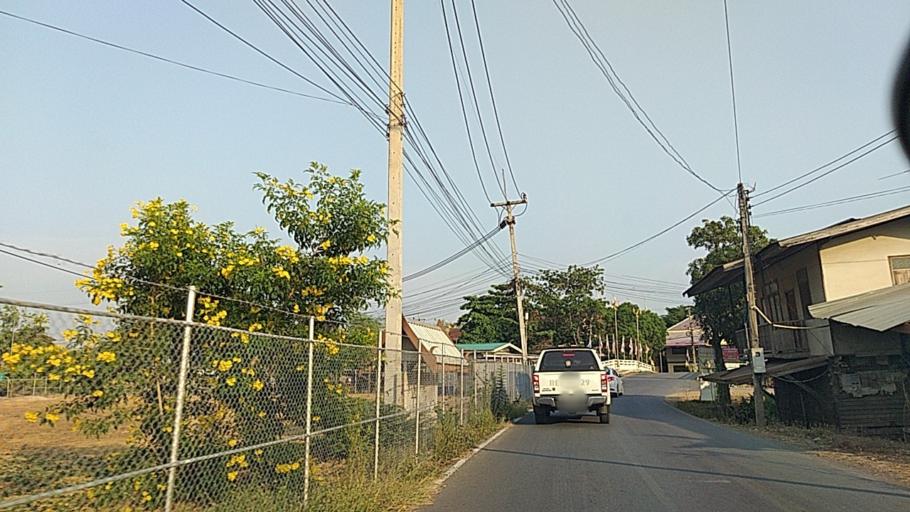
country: TH
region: Sara Buri
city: Nong Khae
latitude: 14.2761
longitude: 100.8216
